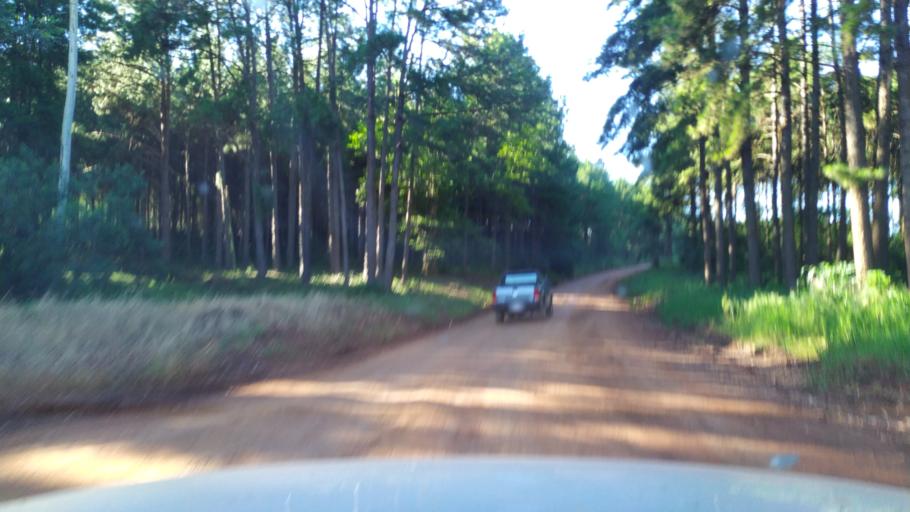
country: AR
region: Misiones
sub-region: Departamento de Montecarlo
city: Montecarlo
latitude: -26.6086
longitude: -54.6987
